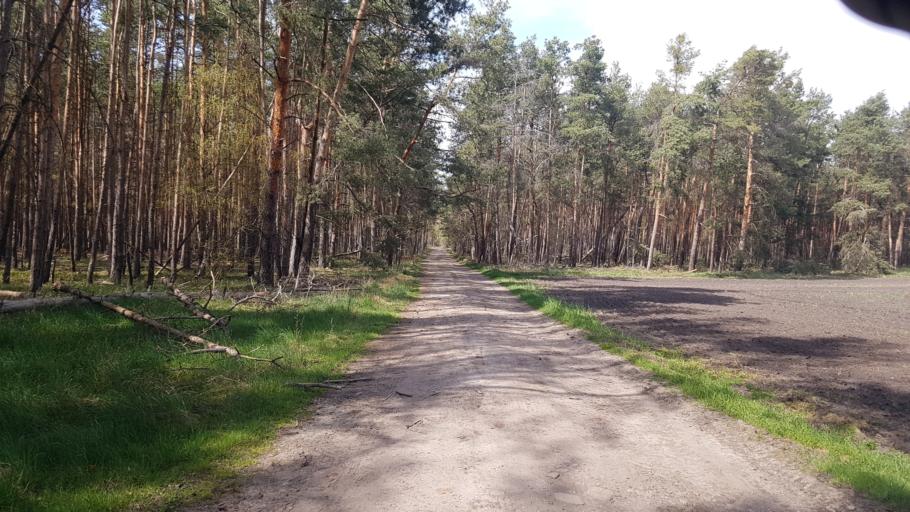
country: DE
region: Brandenburg
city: Plessa
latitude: 51.5424
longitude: 13.6617
